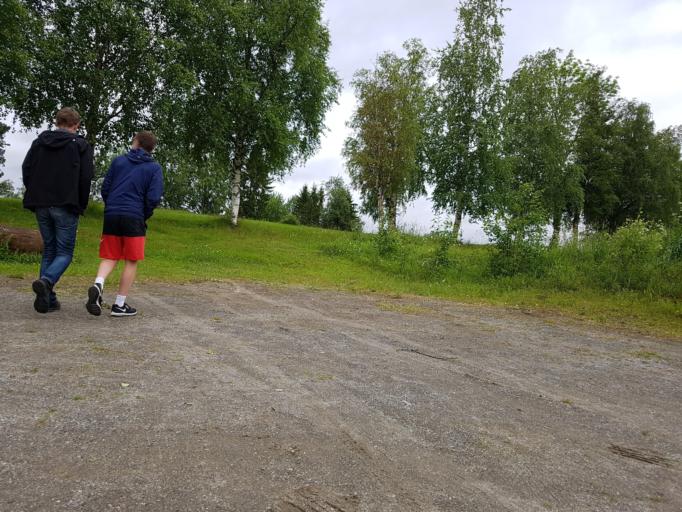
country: NO
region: Sor-Trondelag
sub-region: Selbu
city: Mebonden
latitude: 63.2331
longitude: 11.0297
